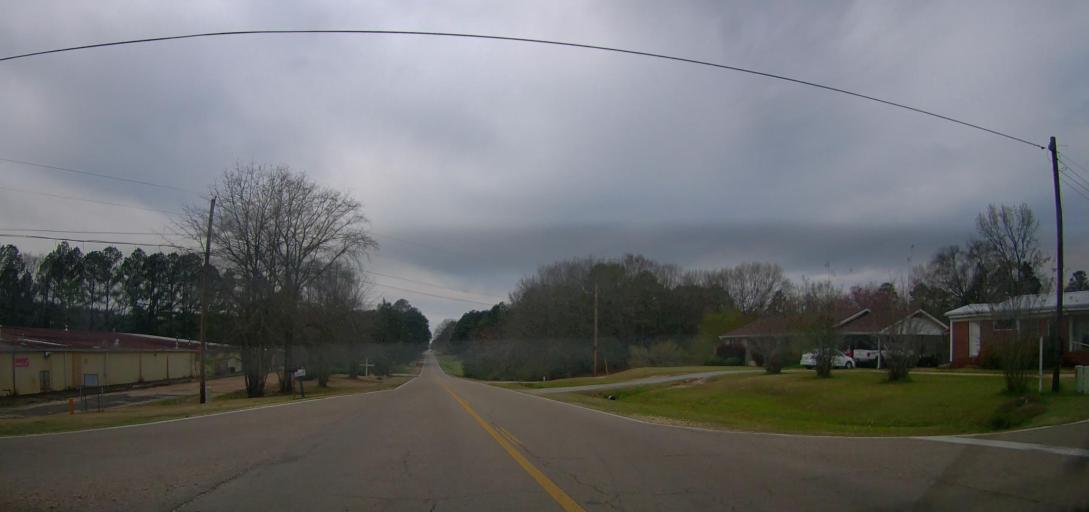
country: US
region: Mississippi
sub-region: Itawamba County
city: Mantachie
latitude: 34.2553
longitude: -88.4920
